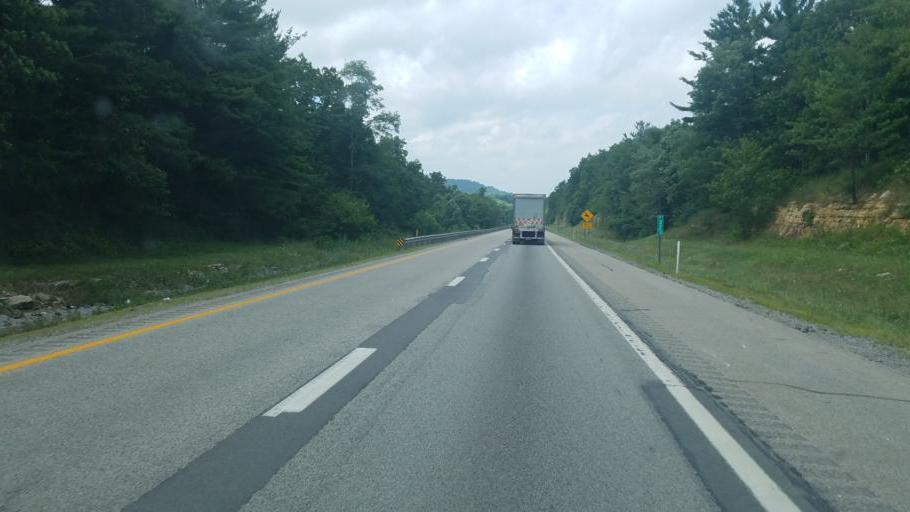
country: US
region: West Virginia
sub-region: Raleigh County
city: Shady Spring
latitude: 37.6574
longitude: -81.1111
